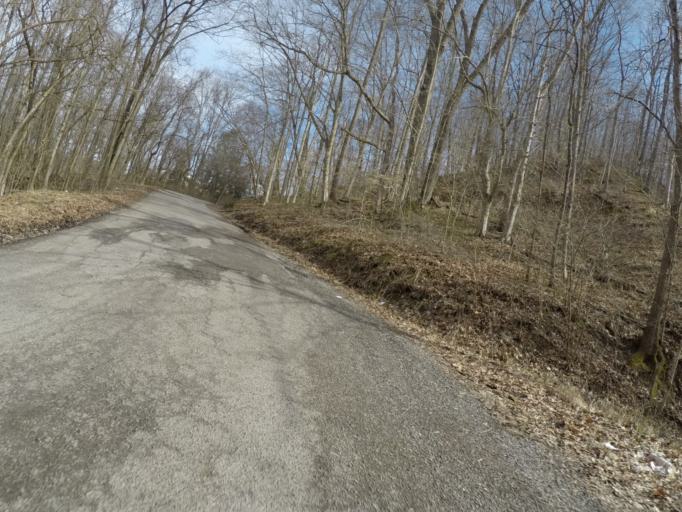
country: US
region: West Virginia
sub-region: Wayne County
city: Lavalette
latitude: 38.3422
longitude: -82.5087
